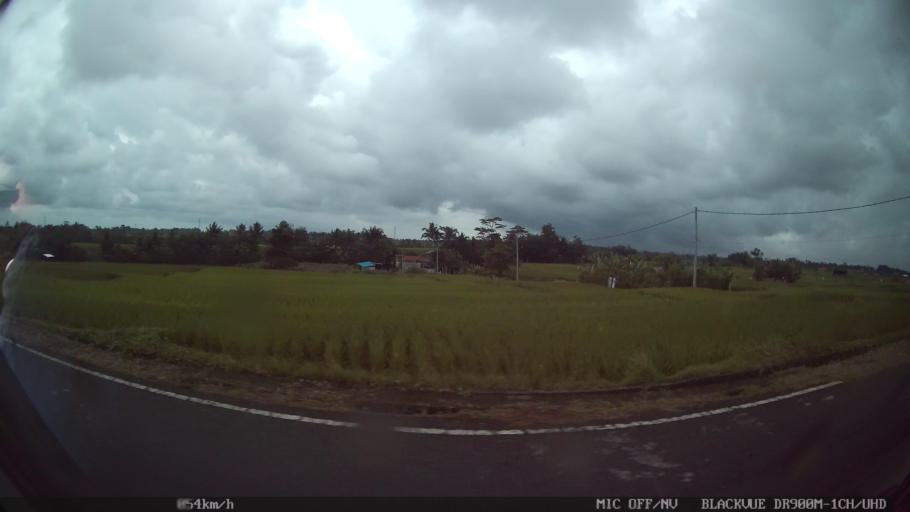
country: ID
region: Bali
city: Banjar Cemenggon
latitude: -8.5365
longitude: 115.1877
